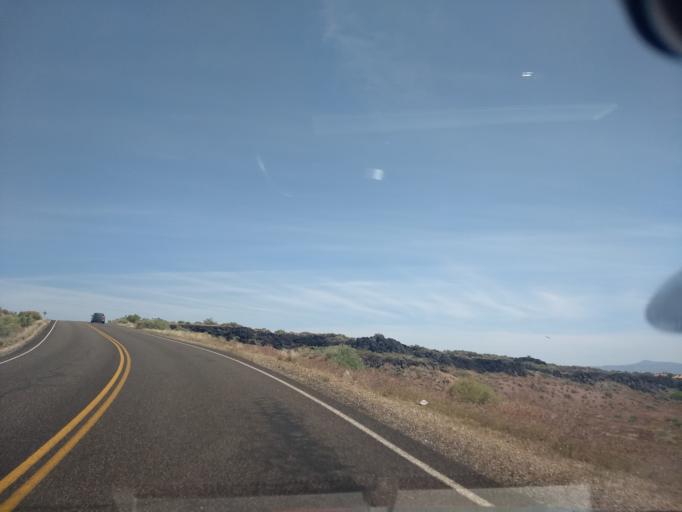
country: US
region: Utah
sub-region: Washington County
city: Santa Clara
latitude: 37.1444
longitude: -113.6514
